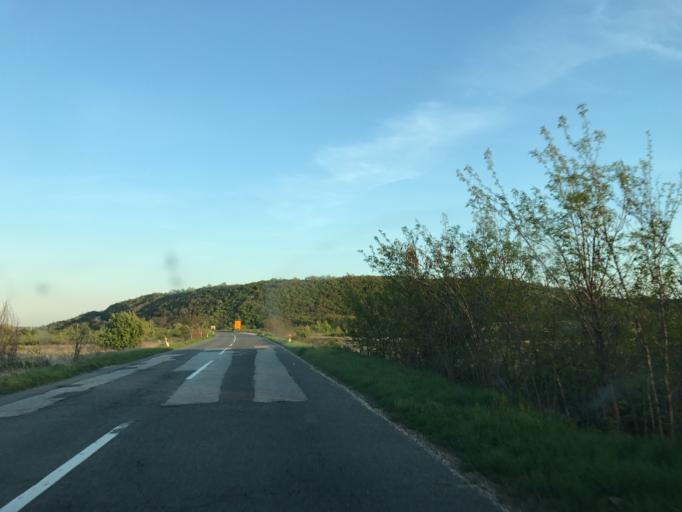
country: RO
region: Mehedinti
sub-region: Comuna Gogosu
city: Ostrovu Mare
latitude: 44.4324
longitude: 22.4626
